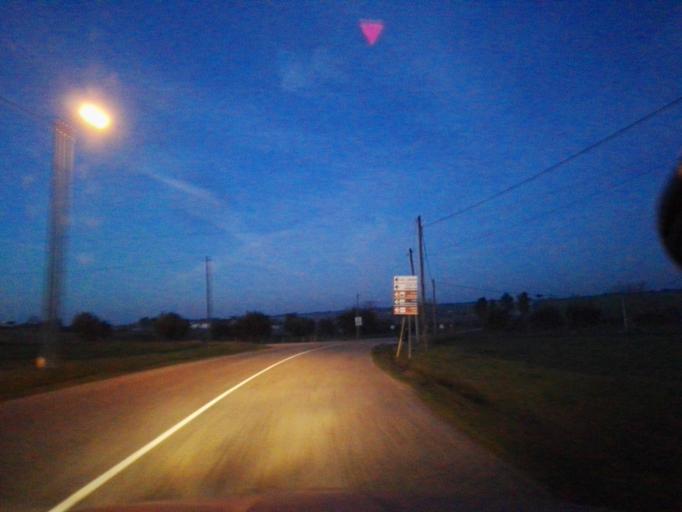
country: PT
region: Evora
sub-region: Arraiolos
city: Arraiolos
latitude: 38.8315
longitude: -7.8353
